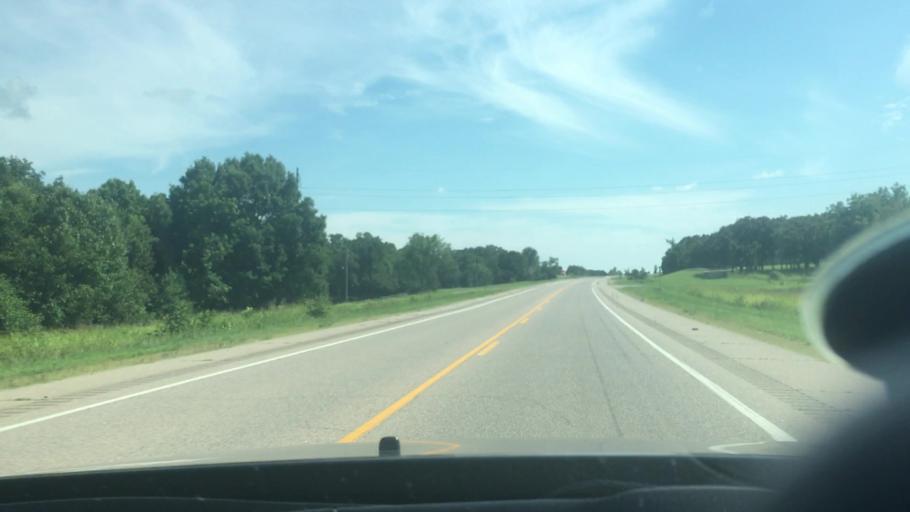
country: US
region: Oklahoma
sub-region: Seminole County
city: Seminole
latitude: 35.1459
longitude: -96.6753
